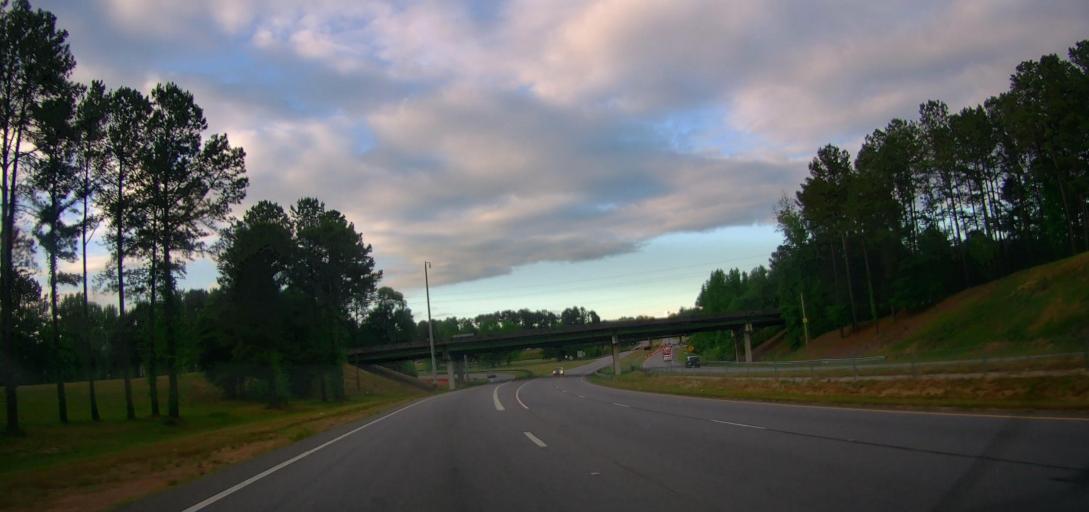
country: US
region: Georgia
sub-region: Clarke County
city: Athens
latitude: 33.9750
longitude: -83.3551
